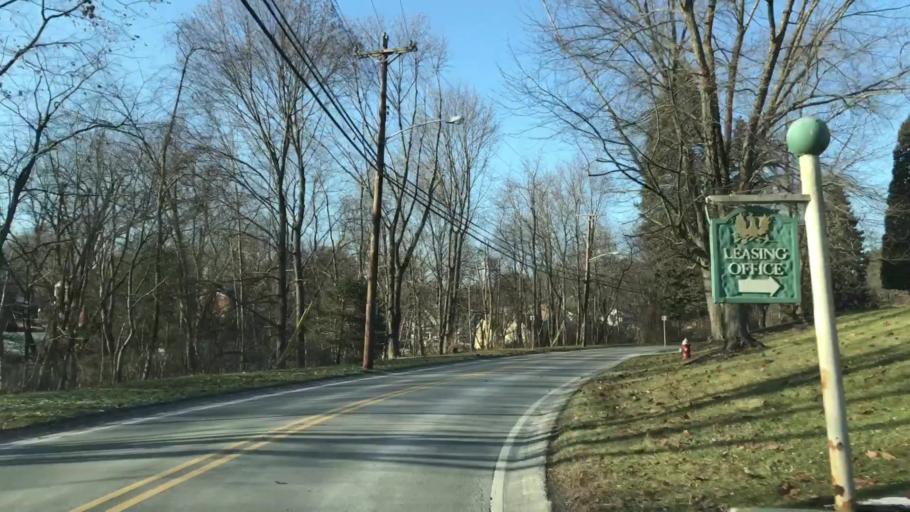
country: US
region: Pennsylvania
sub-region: Allegheny County
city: Allison Park
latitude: 40.5836
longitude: -79.9990
